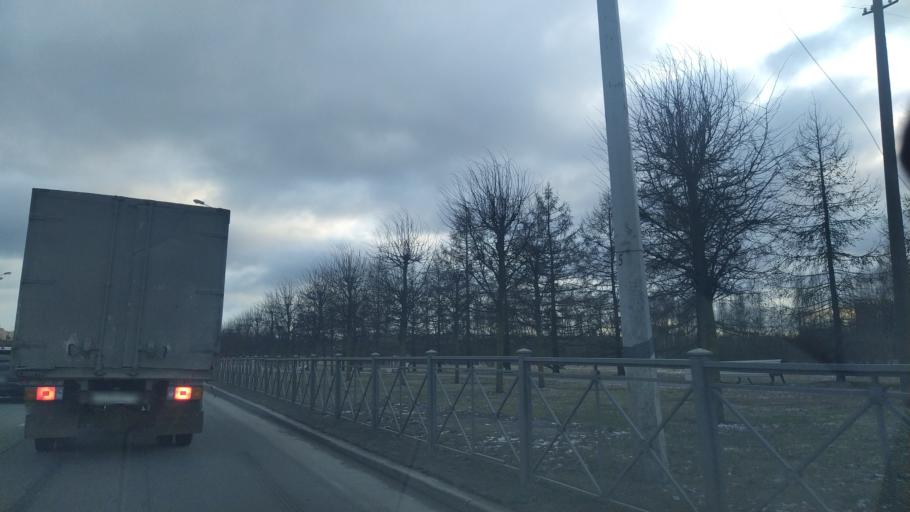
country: RU
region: St.-Petersburg
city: Pushkin
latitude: 59.7393
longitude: 30.3936
